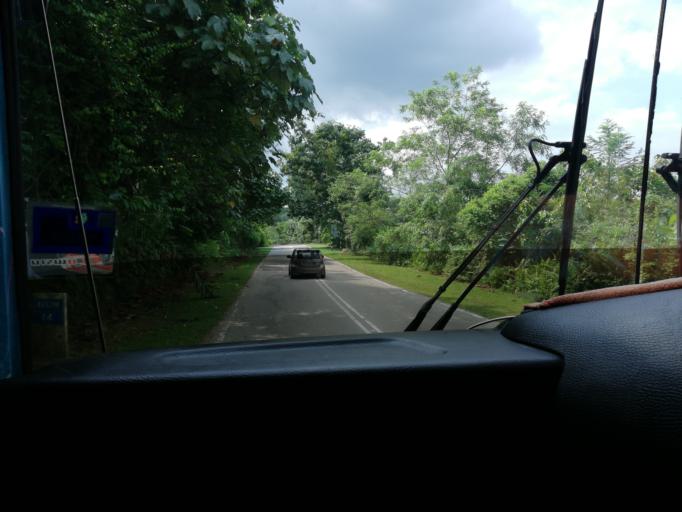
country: MY
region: Kedah
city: Kulim
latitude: 5.3183
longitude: 100.6002
